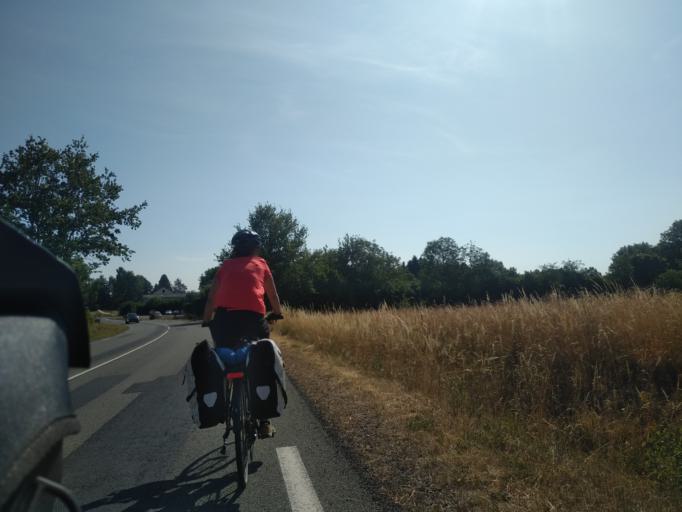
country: FR
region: Auvergne
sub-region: Departement du Puy-de-Dome
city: Saint-Georges-de-Mons
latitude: 45.9423
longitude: 2.8405
